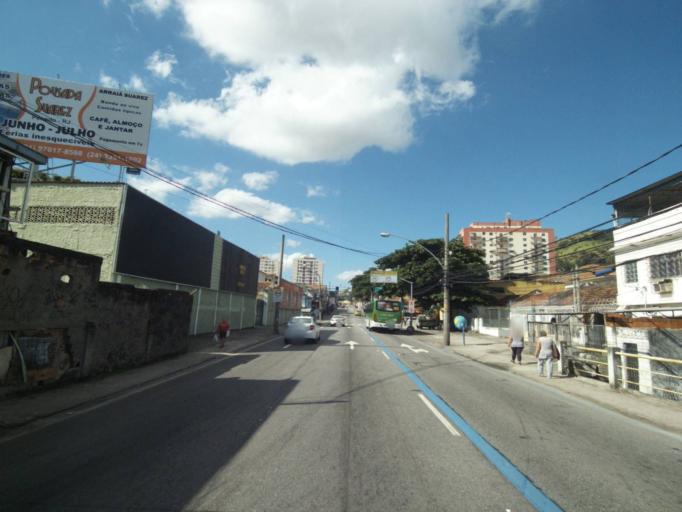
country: BR
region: Rio de Janeiro
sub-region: Rio De Janeiro
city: Rio de Janeiro
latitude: -22.9051
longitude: -43.2691
